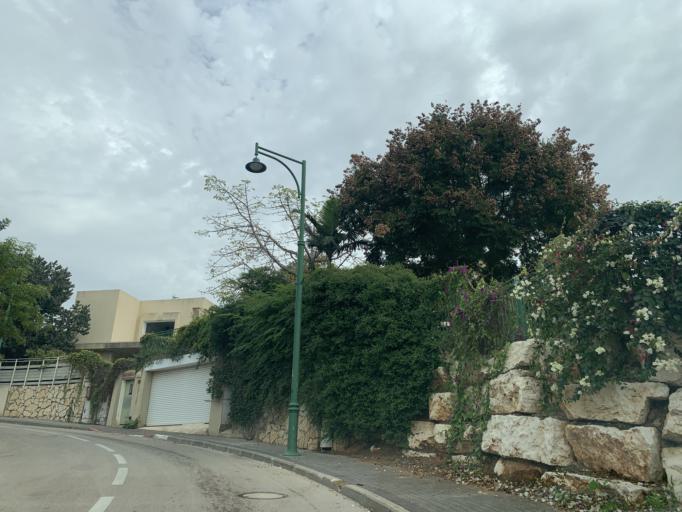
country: IL
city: Nirit
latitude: 32.1486
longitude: 34.9861
